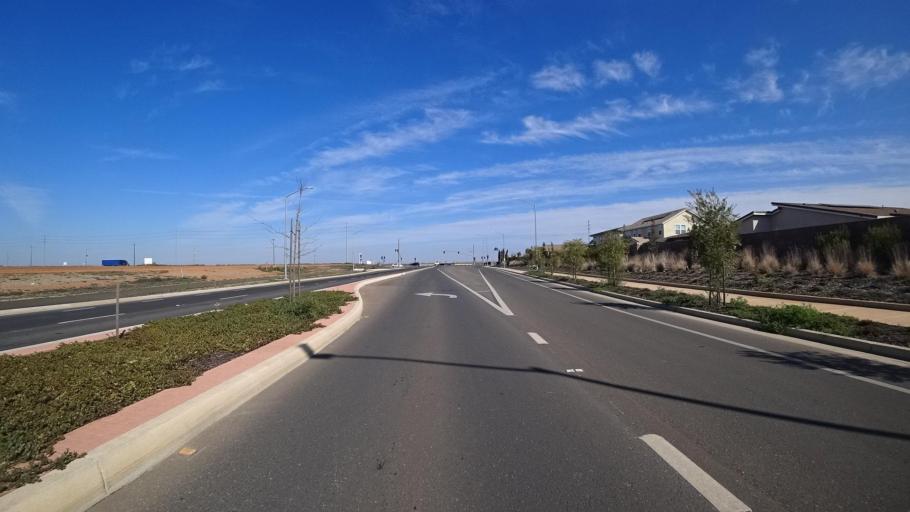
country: US
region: California
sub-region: Sacramento County
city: Gold River
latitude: 38.5577
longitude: -121.2242
